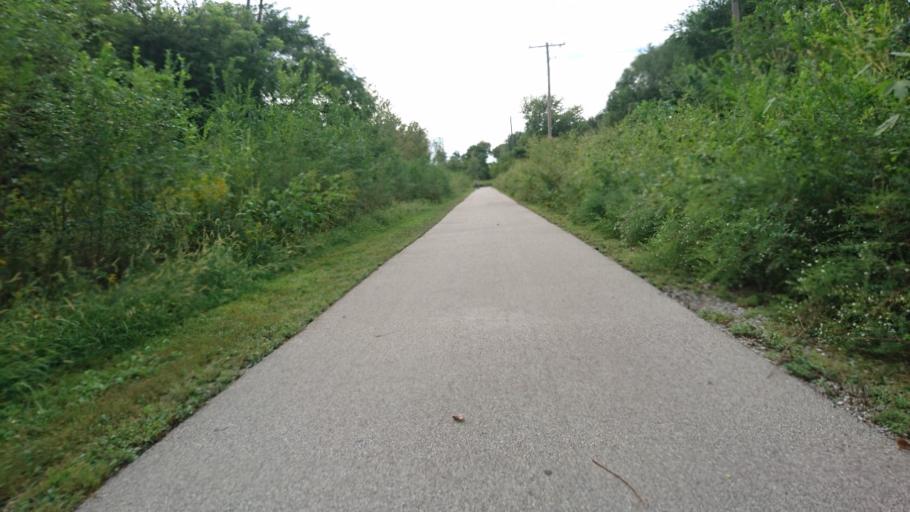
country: US
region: Illinois
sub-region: Sangamon County
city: Jerome
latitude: 39.7568
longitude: -89.6715
